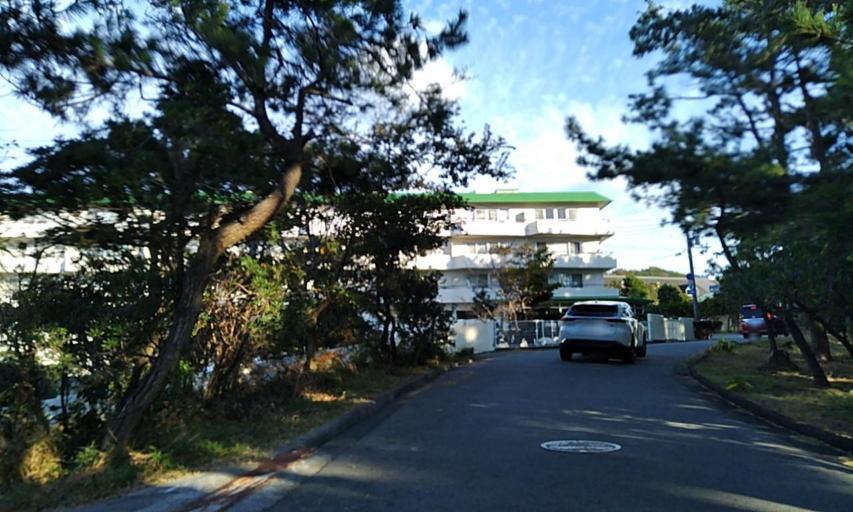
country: JP
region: Wakayama
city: Tanabe
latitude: 33.6713
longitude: 135.3317
